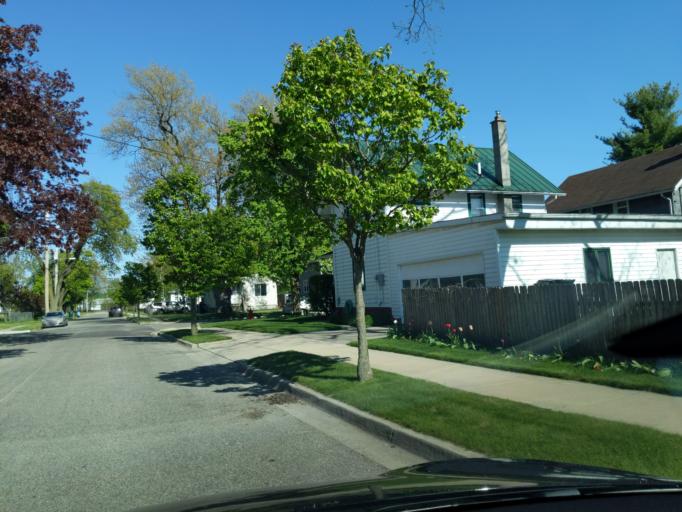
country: US
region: Michigan
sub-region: Ingham County
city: Lansing
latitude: 42.7111
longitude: -84.5622
